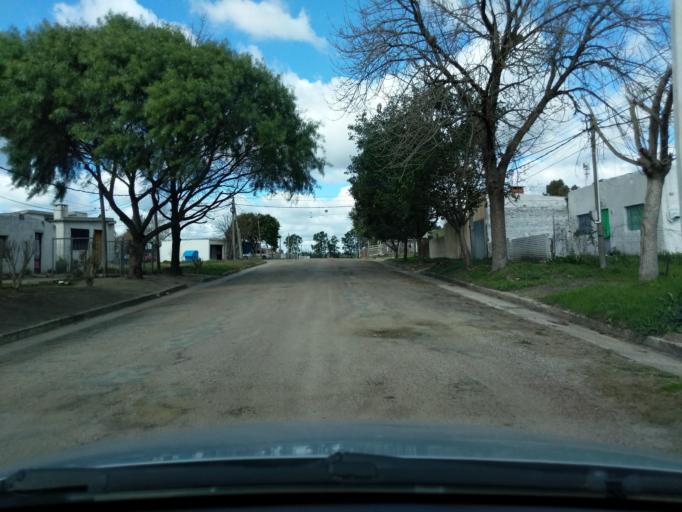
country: UY
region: Florida
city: Florida
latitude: -34.0937
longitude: -56.2316
